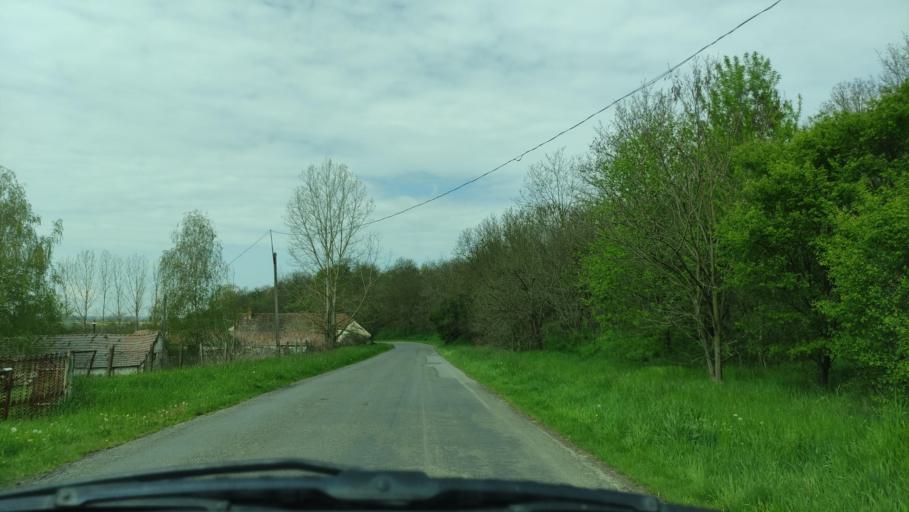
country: HU
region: Baranya
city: Sasd
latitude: 46.3062
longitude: 18.1565
